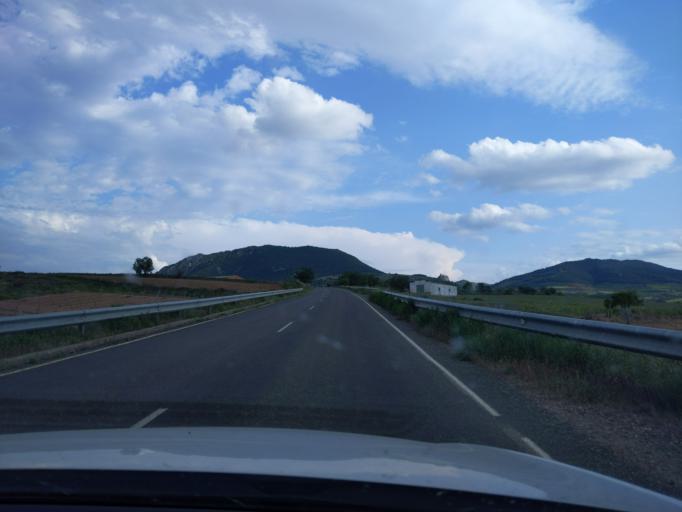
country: ES
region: La Rioja
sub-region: Provincia de La Rioja
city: Clavijo
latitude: 42.3767
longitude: -2.4235
